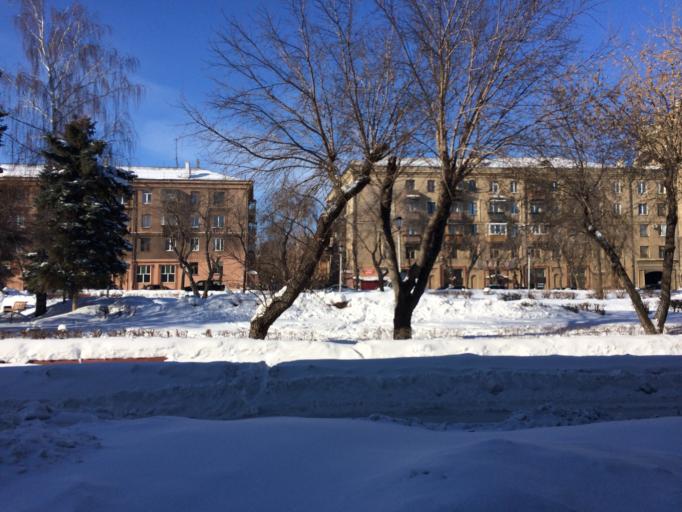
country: RU
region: Chelyabinsk
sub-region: Gorod Magnitogorsk
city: Magnitogorsk
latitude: 53.4212
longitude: 58.9966
